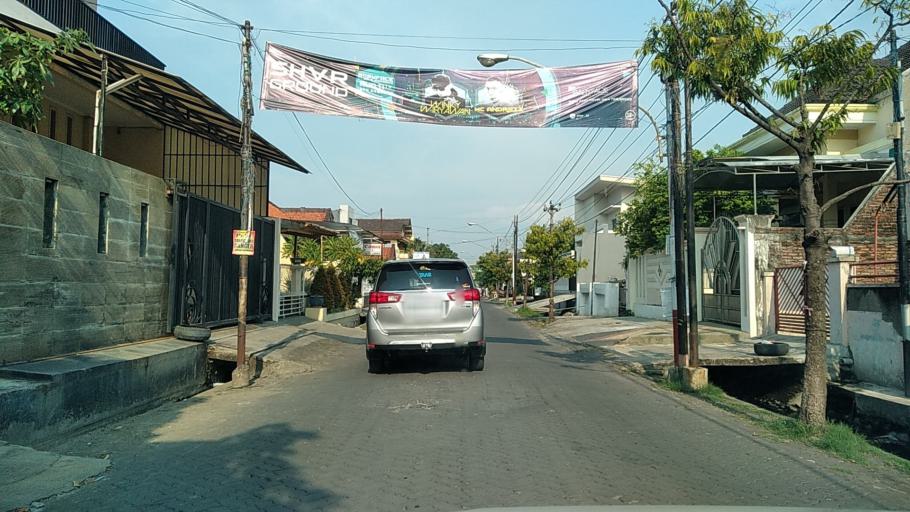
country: ID
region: Central Java
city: Semarang
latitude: -6.9595
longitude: 110.4059
